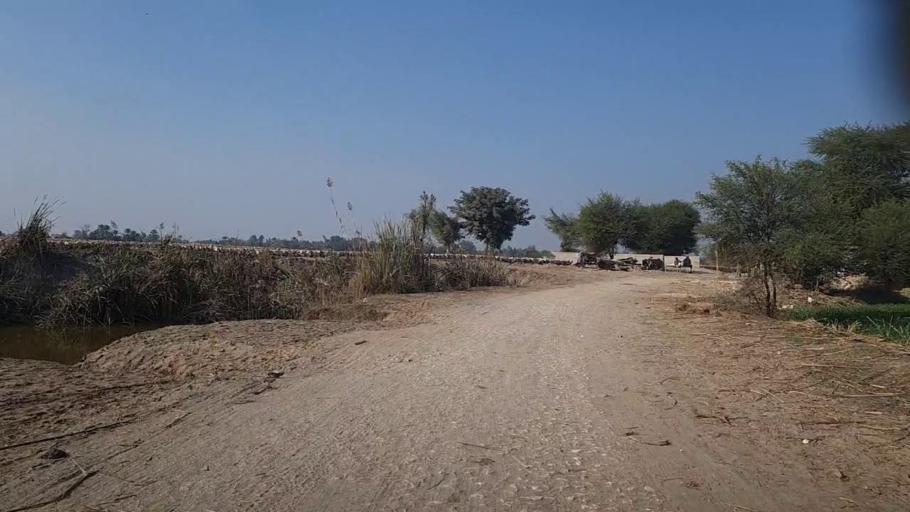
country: PK
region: Sindh
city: Mirpur Mathelo
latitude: 27.8999
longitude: 69.6435
